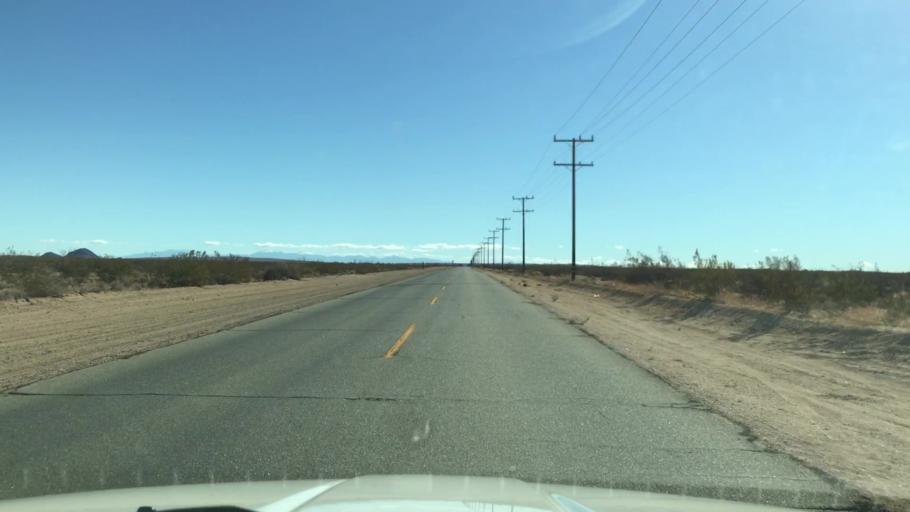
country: US
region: California
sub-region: Kern County
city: California City
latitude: 35.1751
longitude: -117.9858
